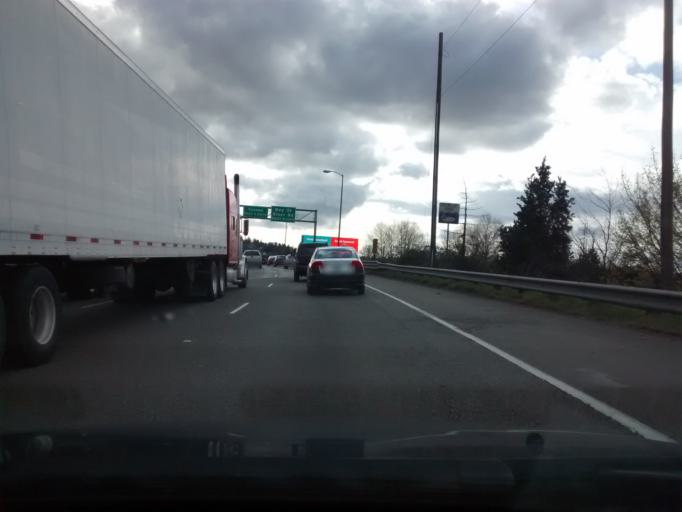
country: US
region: Washington
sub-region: Pierce County
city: Fife
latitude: 47.2419
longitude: -122.3974
